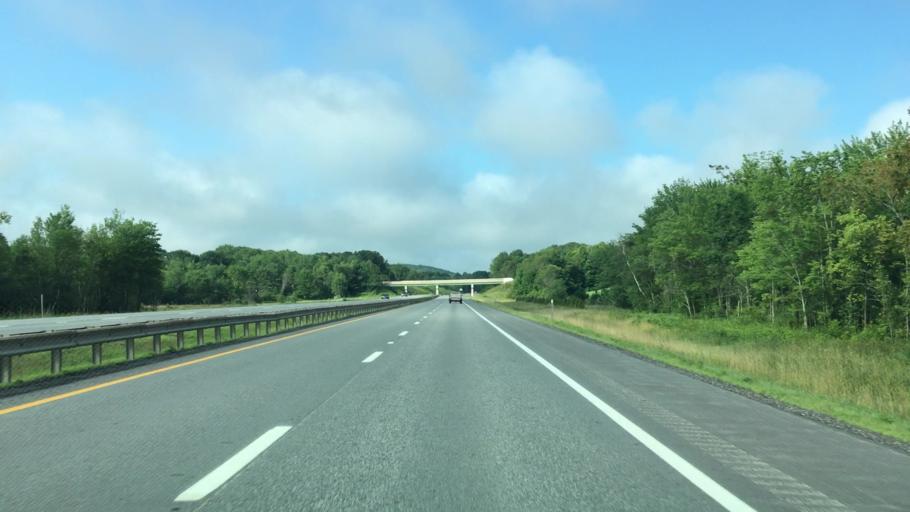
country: US
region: Maine
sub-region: Androscoggin County
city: Sabattus
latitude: 44.0862
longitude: -70.1084
